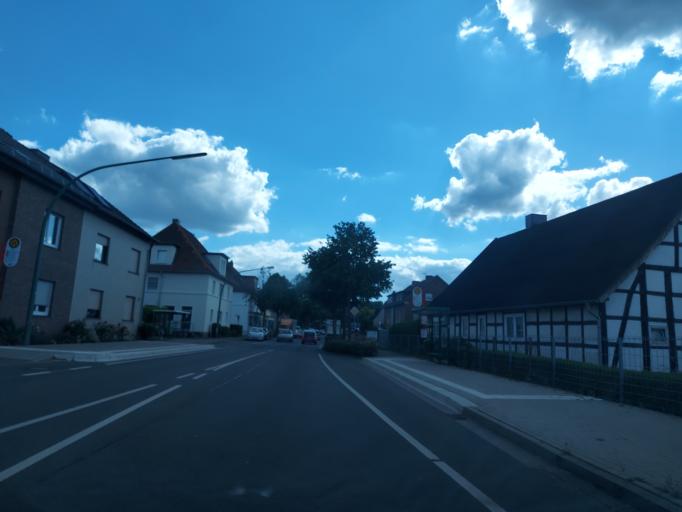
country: DE
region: Lower Saxony
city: Hagen
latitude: 52.2245
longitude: 8.0098
